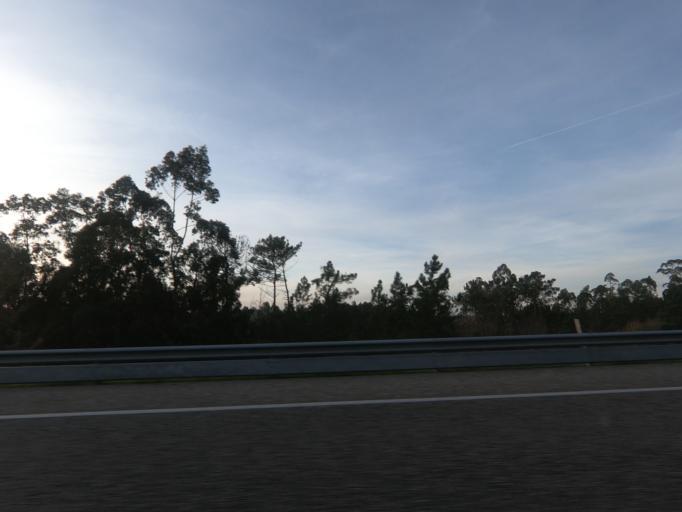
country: PT
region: Coimbra
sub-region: Soure
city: Soure
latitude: 40.0311
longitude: -8.5863
